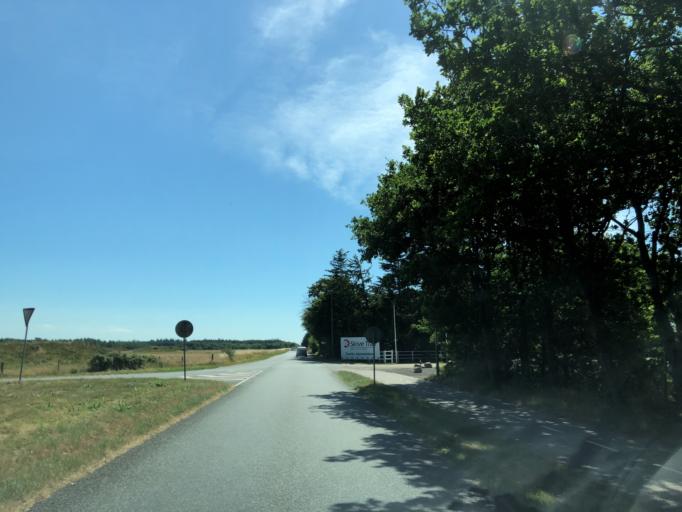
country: DK
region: Central Jutland
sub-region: Skive Kommune
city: Skive
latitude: 56.5321
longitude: 9.0377
